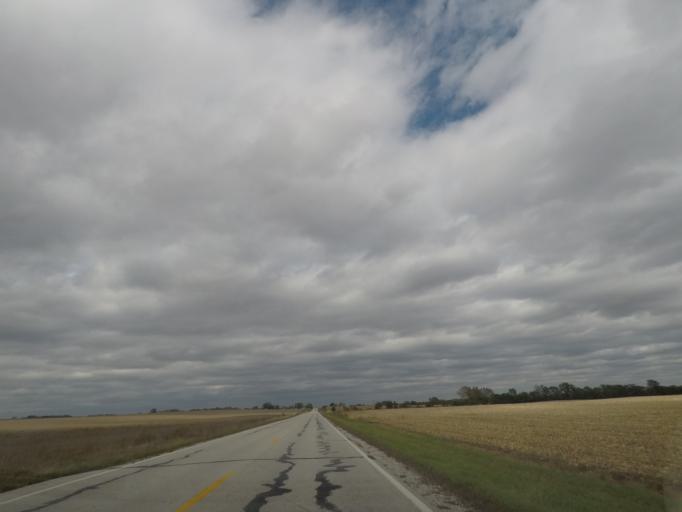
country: US
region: Iowa
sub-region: Story County
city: Huxley
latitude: 41.8529
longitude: -93.5316
